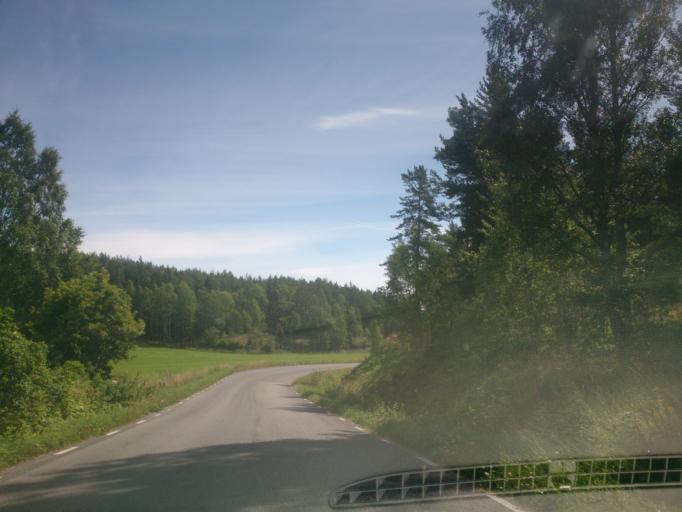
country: SE
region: OEstergoetland
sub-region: Valdemarsviks Kommun
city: Valdemarsvik
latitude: 58.2978
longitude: 16.6624
